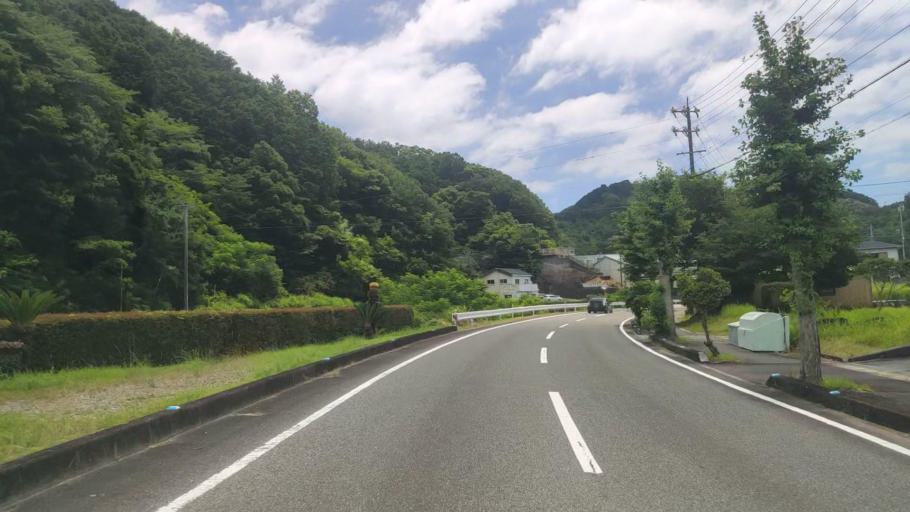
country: JP
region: Mie
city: Owase
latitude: 34.2262
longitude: 136.3944
